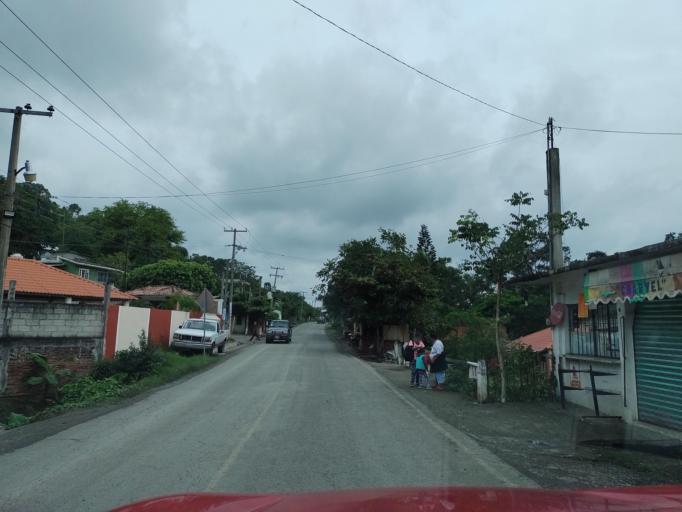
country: MX
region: Puebla
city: Espinal
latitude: 20.2626
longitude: -97.3549
